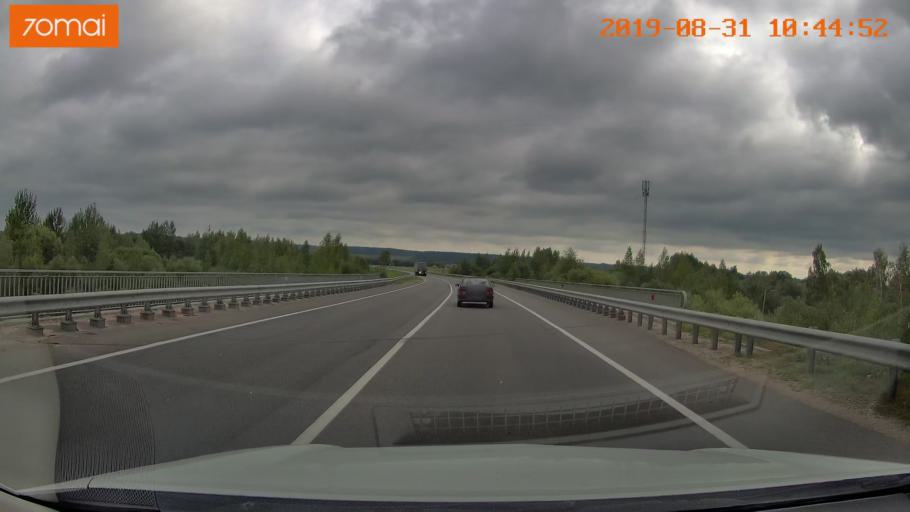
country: BY
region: Mogilev
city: Palykavichy Pyershyya
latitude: 53.9700
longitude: 30.3651
